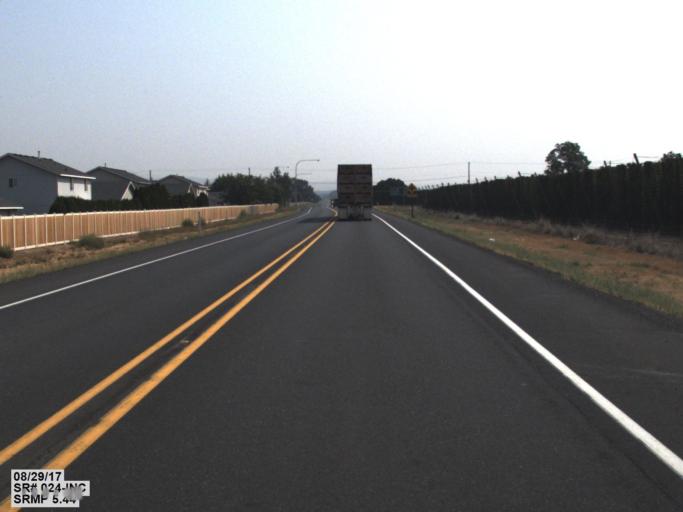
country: US
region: Washington
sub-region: Yakima County
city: Terrace Heights
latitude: 46.5494
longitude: -120.3788
